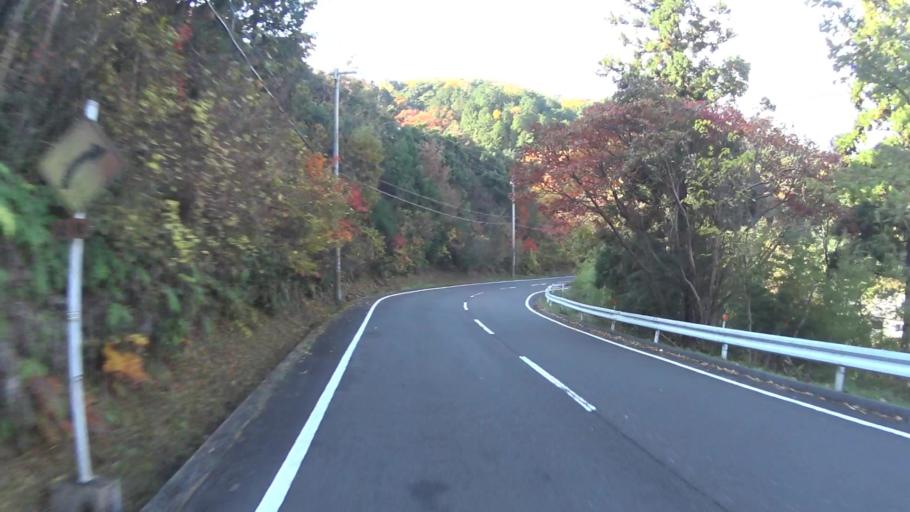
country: JP
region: Kyoto
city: Maizuru
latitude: 35.5484
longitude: 135.3955
